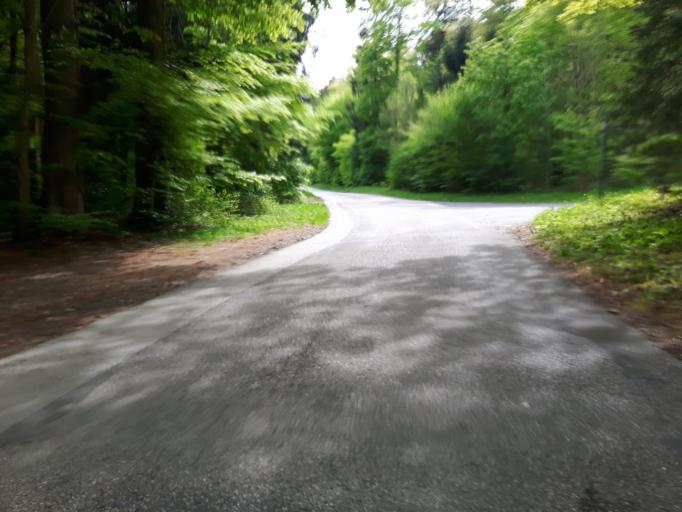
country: CH
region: Neuchatel
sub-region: Boudry District
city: Bevaix
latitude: 46.9233
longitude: 6.8037
